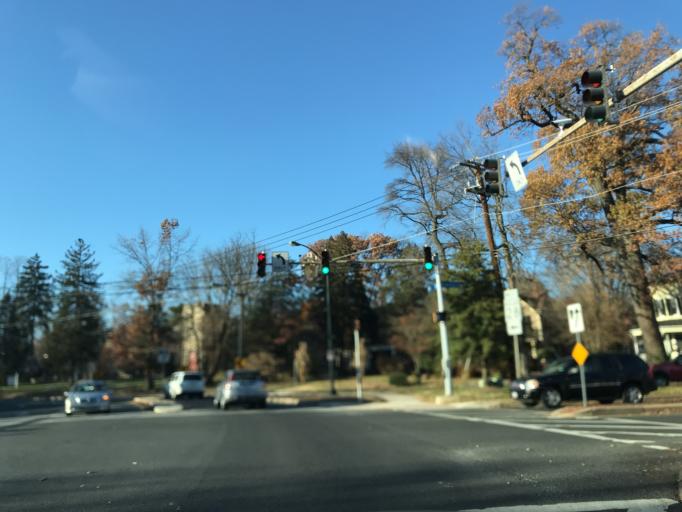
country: US
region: Maryland
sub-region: Montgomery County
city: Rockville
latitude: 39.0837
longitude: -77.1566
